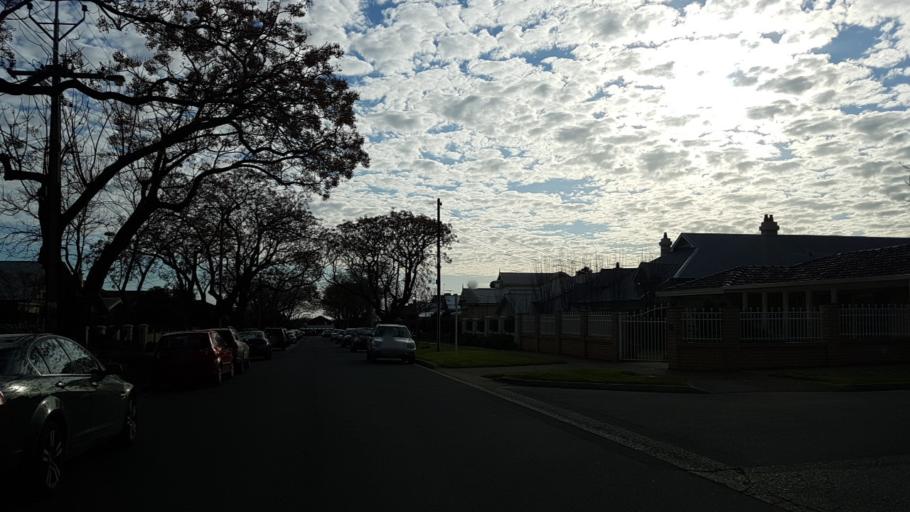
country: AU
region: South Australia
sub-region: Prospect
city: Prospect
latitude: -34.8870
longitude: 138.5967
